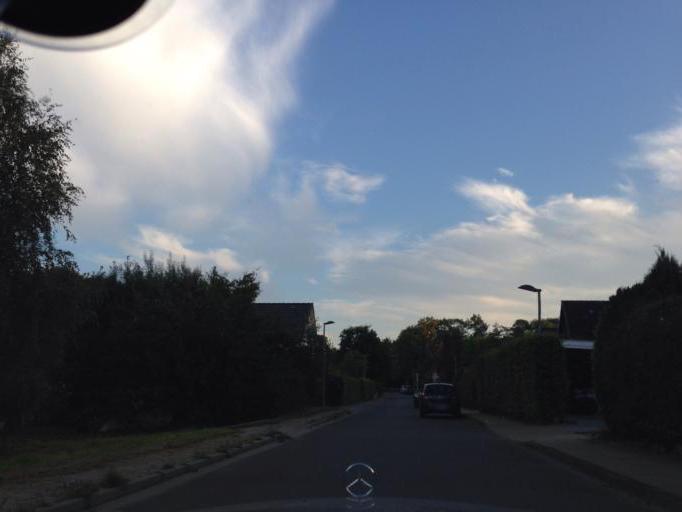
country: DE
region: Schleswig-Holstein
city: Ahrensburg
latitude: 53.6816
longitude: 10.2204
